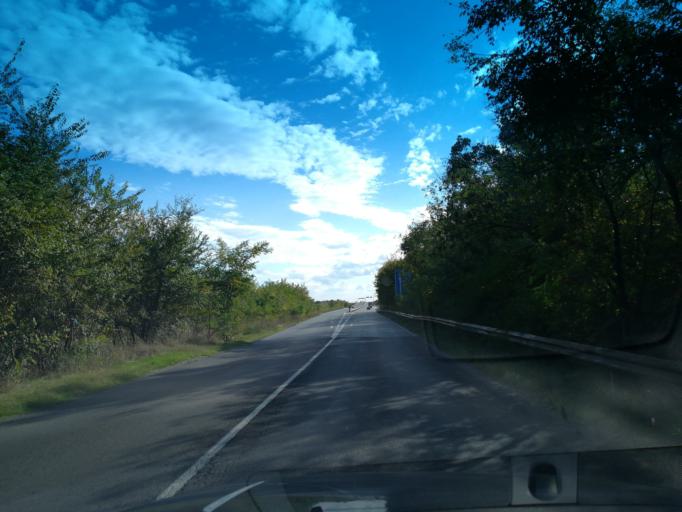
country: BG
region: Stara Zagora
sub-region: Obshtina Stara Zagora
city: Stara Zagora
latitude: 42.3466
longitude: 25.6598
